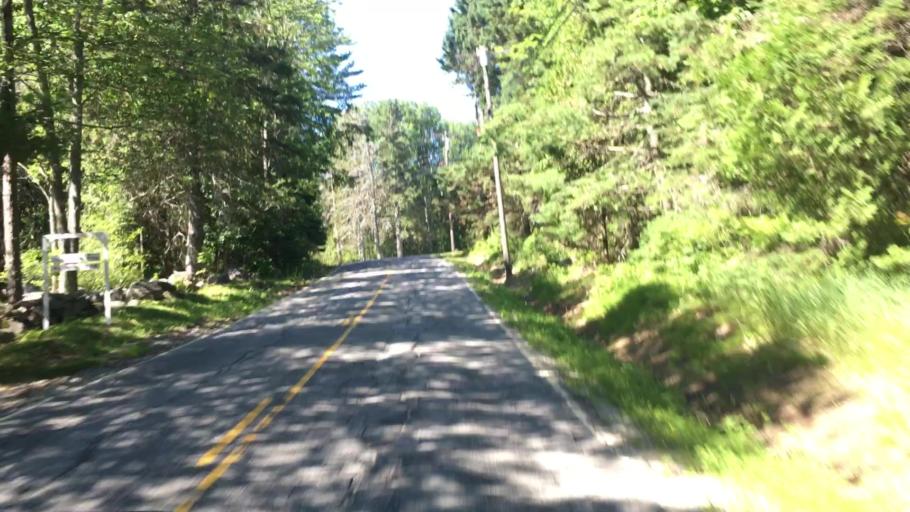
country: US
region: Maine
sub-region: Hancock County
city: Sedgwick
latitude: 44.3249
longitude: -68.6063
